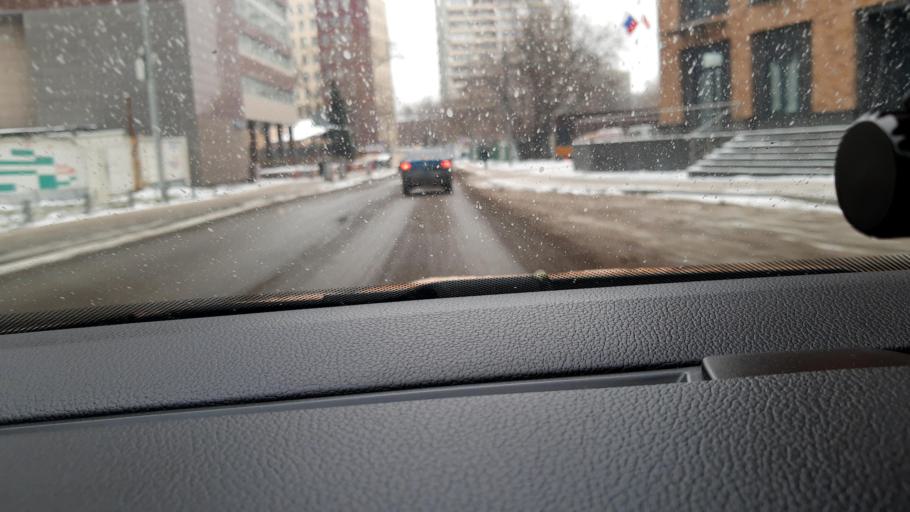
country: RU
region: Moscow
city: Sokol'niki
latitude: 55.8098
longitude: 37.6443
